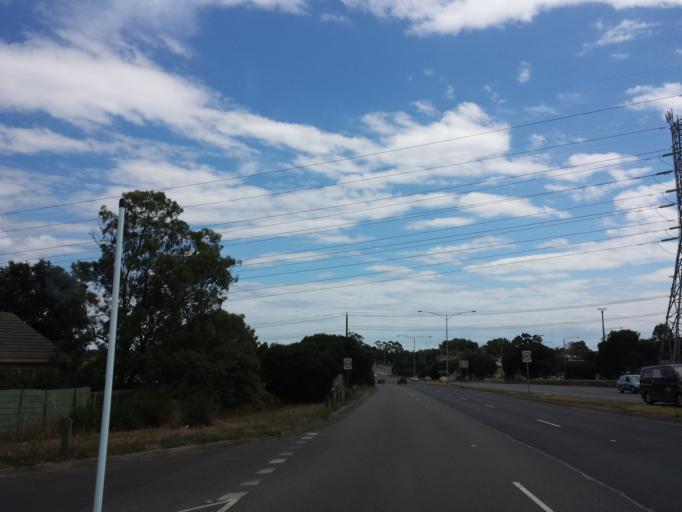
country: AU
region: Victoria
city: Watsonia
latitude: -37.7111
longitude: 145.0849
